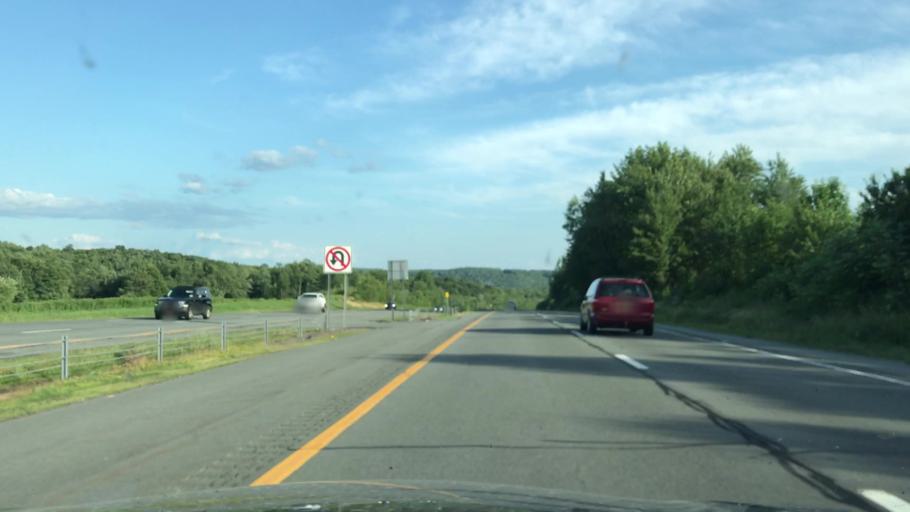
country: US
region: New York
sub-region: Sullivan County
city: Liberty
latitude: 41.7388
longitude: -74.7313
